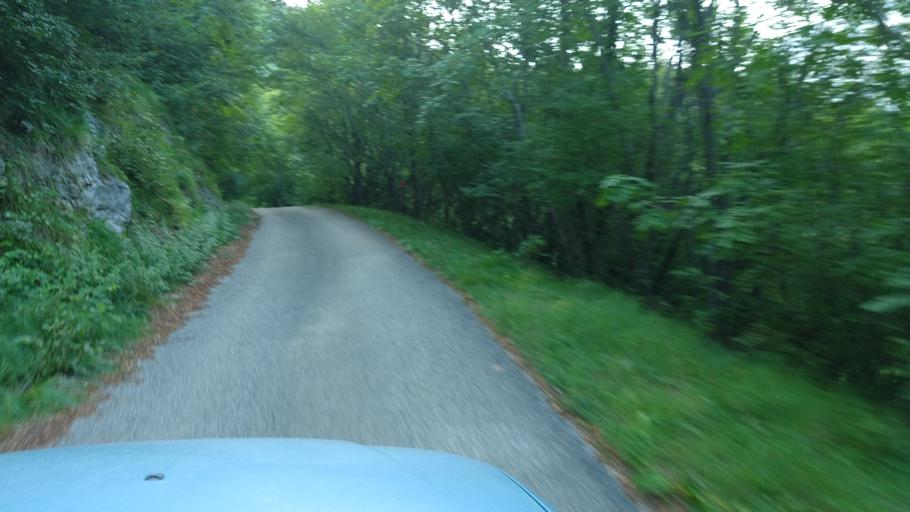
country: IT
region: Veneto
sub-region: Provincia di Vicenza
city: Campolongo sul Brenta
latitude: 45.8273
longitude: 11.6887
